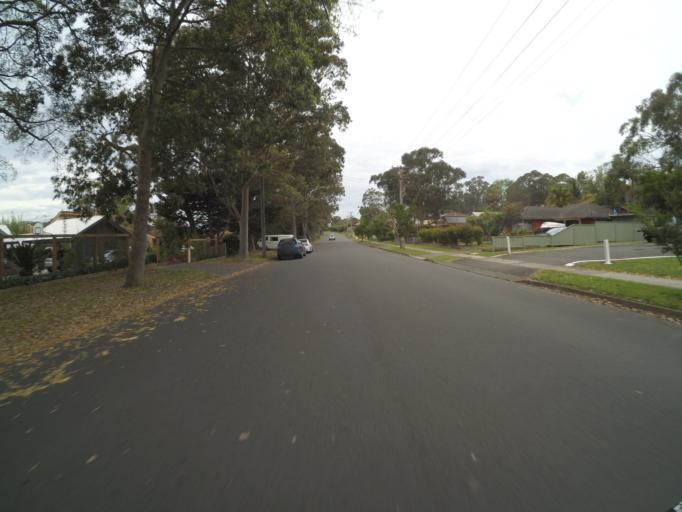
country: AU
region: New South Wales
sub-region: Kiama
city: Jamberoo
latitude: -34.6490
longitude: 150.7808
